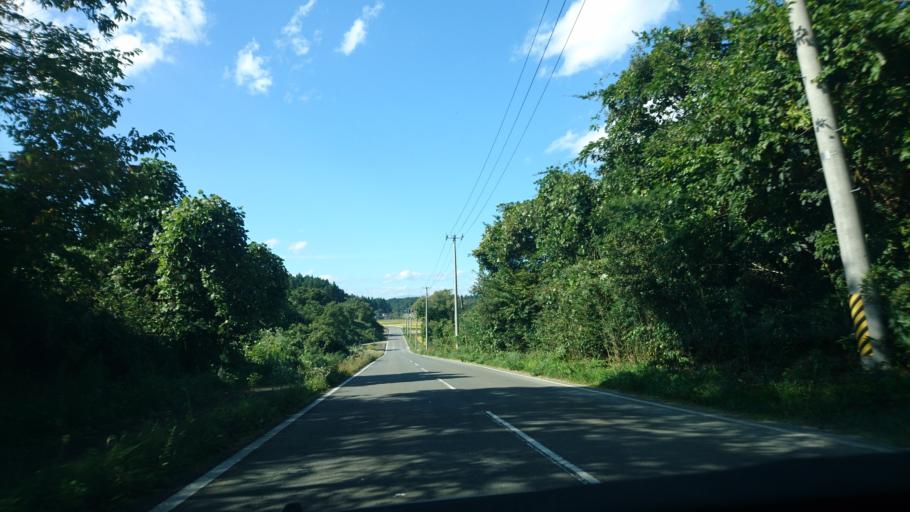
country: JP
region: Iwate
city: Ichinoseki
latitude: 38.8586
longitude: 141.0505
